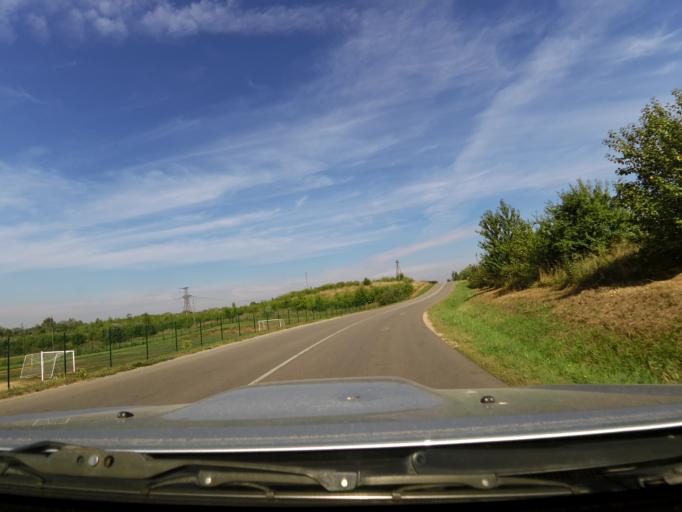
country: LT
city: Grigiskes
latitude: 54.7839
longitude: 25.0877
